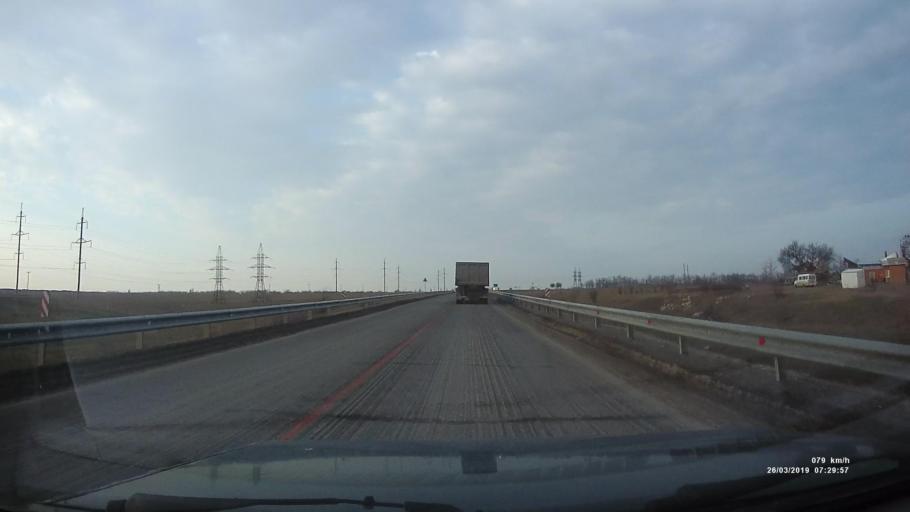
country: RU
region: Rostov
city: Novobessergenovka
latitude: 47.2404
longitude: 38.8121
